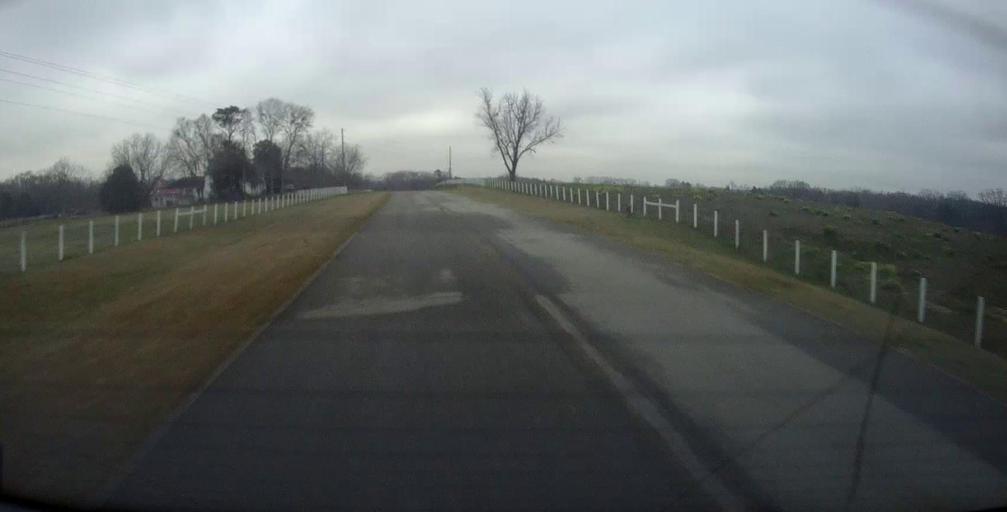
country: US
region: Georgia
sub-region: Lamar County
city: Barnesville
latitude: 33.0146
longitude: -84.1128
